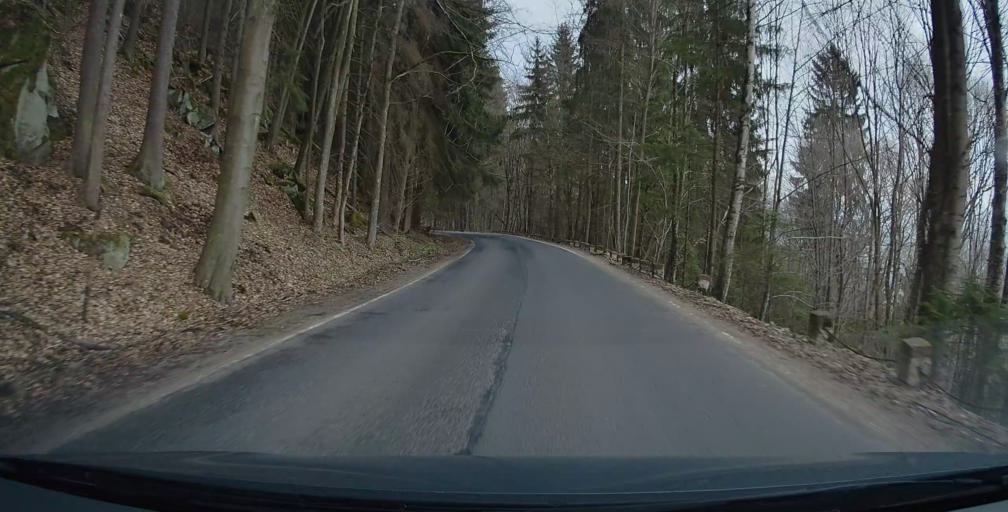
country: PL
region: Lower Silesian Voivodeship
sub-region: Powiat klodzki
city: Radkow
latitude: 50.4810
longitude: 16.3851
